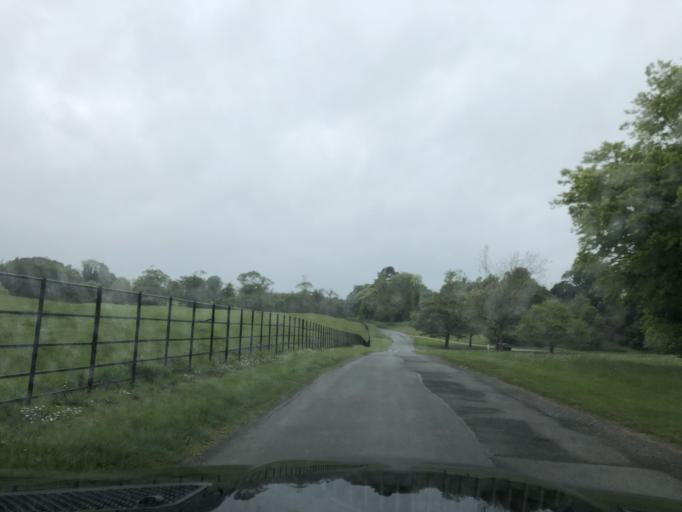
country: GB
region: Northern Ireland
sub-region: Down District
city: Portaferry
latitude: 54.3650
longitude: -5.5818
